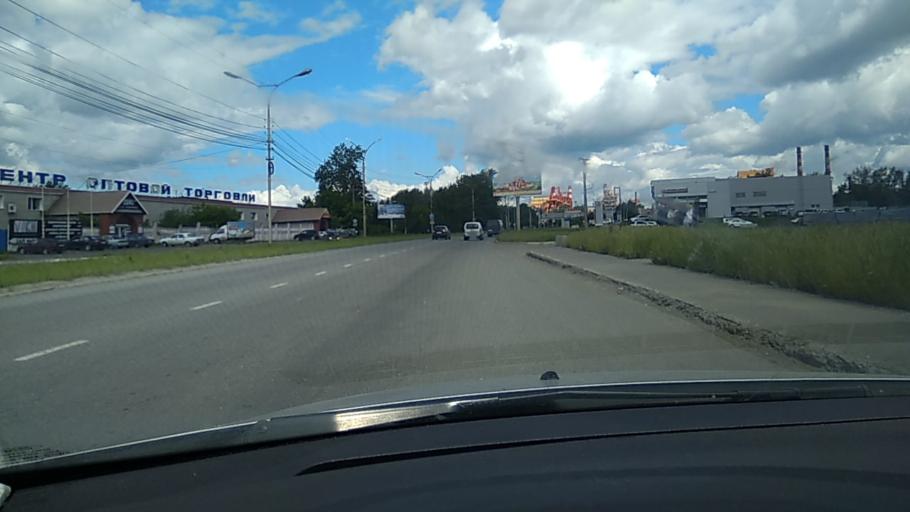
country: RU
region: Sverdlovsk
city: Nizhniy Tagil
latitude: 57.9061
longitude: 60.0097
